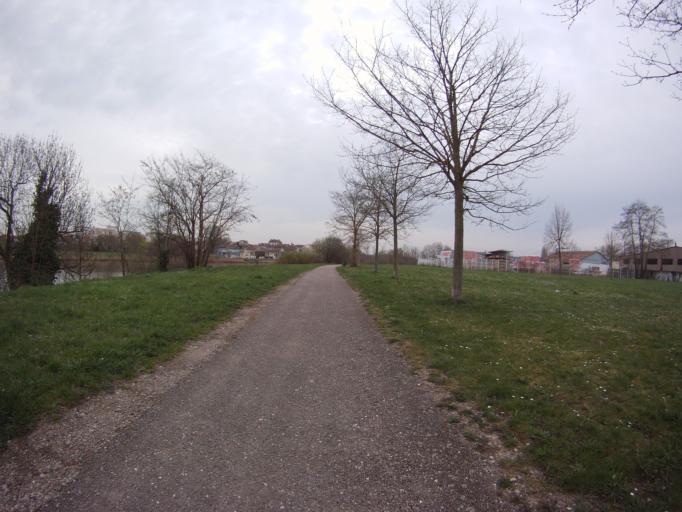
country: FR
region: Lorraine
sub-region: Departement de Meurthe-et-Moselle
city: Tomblaine
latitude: 48.6901
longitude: 6.2046
